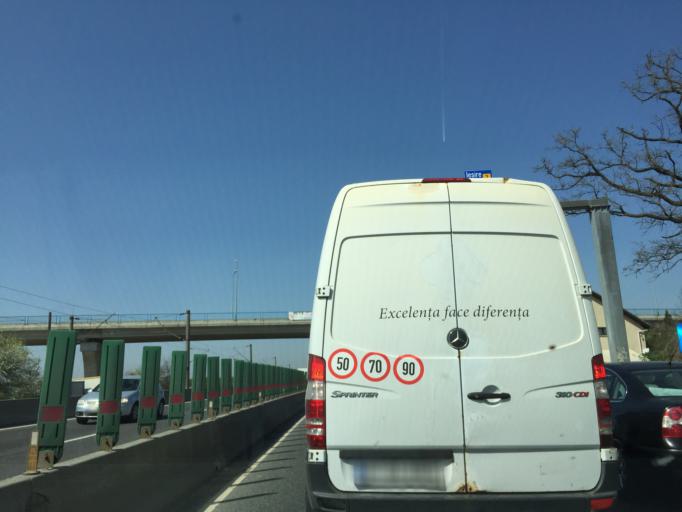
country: RO
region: Ilfov
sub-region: Comuna Tunari
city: Tunari
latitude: 44.5355
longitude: 26.1436
